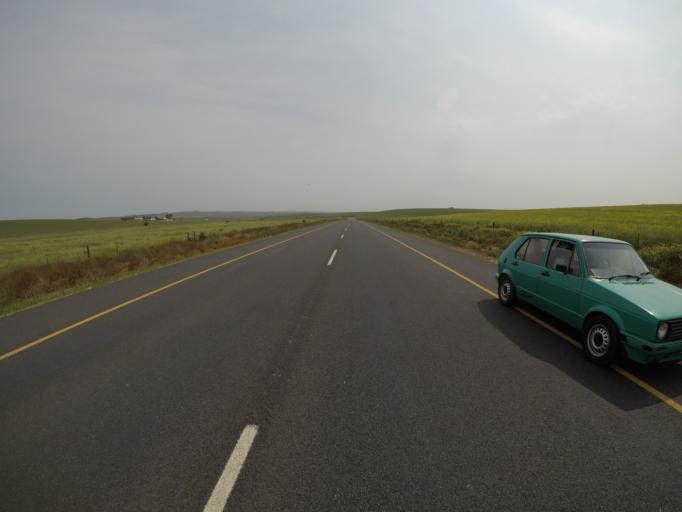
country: ZA
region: Western Cape
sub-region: West Coast District Municipality
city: Malmesbury
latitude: -33.4600
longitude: 18.7854
